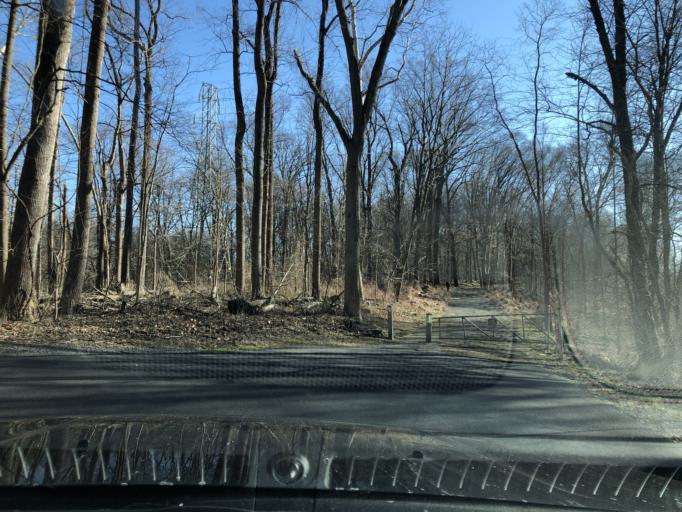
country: US
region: Pennsylvania
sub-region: Lancaster County
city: Lancaster
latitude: 40.0149
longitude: -76.2833
